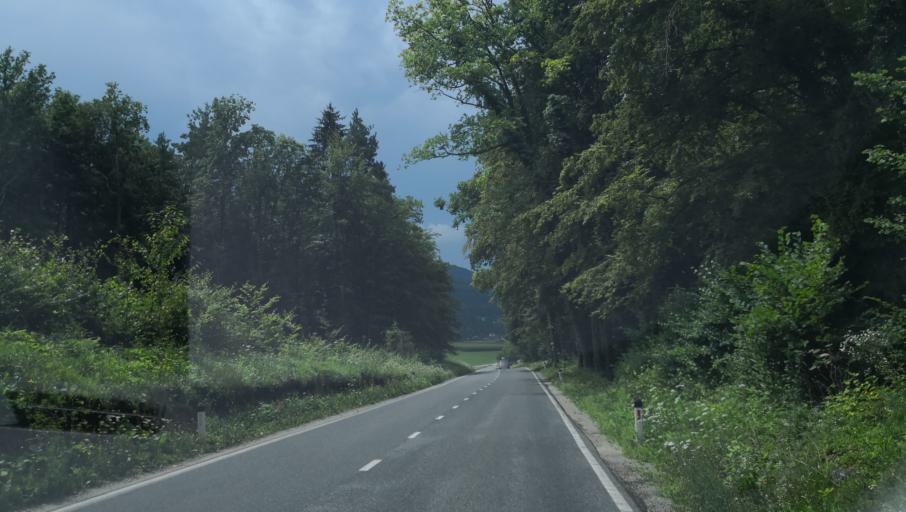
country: SI
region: Ivancna Gorica
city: Ivancna Gorica
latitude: 45.8904
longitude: 14.7971
